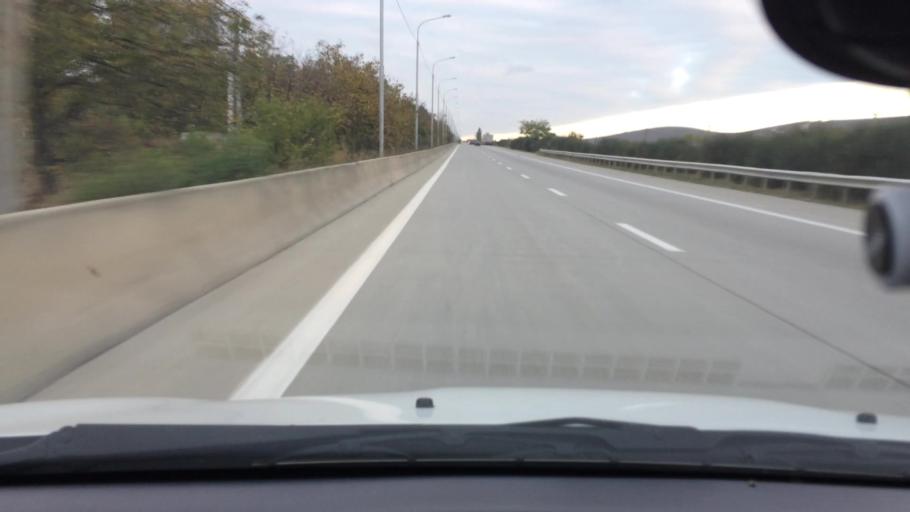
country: GE
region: Shida Kartli
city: Kaspi
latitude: 41.9688
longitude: 44.4589
